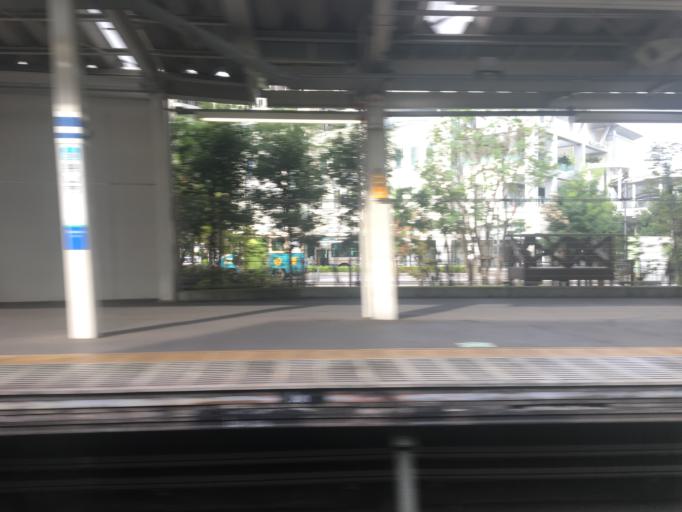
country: JP
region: Saitama
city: Sayama
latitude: 35.8570
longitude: 139.4135
